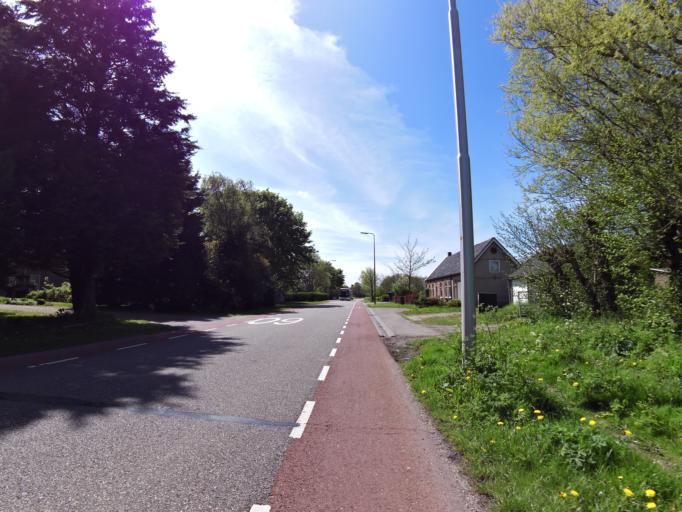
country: NL
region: South Holland
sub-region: Gemeente Hellevoetsluis
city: Nieuw-Helvoet
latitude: 51.8877
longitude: 4.0836
